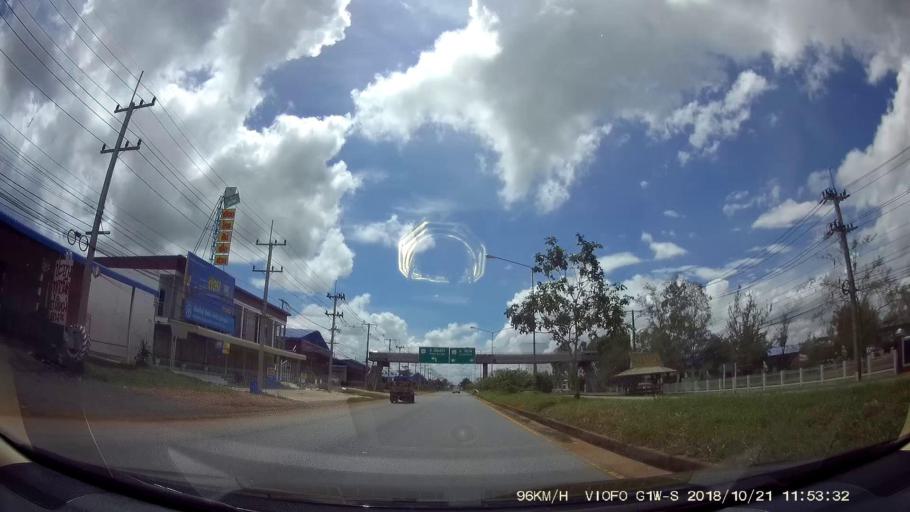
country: TH
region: Chaiyaphum
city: Chatturat
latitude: 15.5945
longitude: 101.9055
